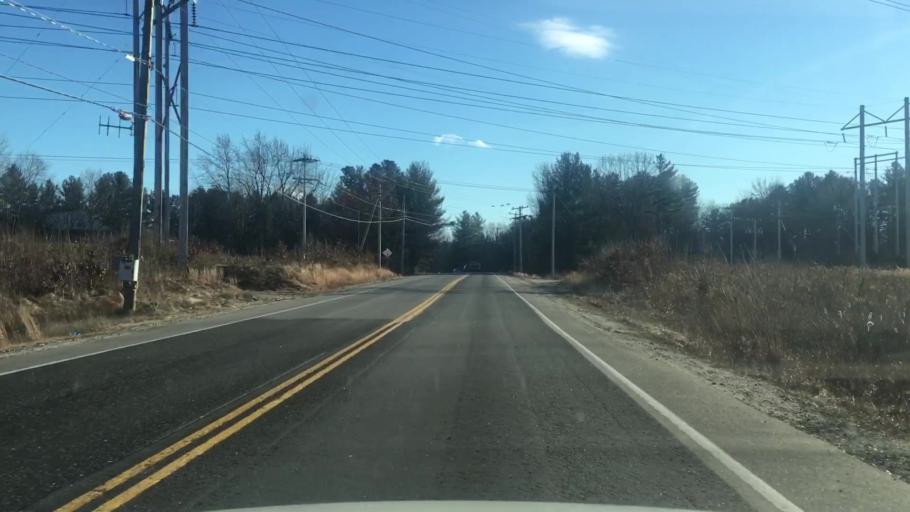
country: US
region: New Hampshire
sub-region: Rockingham County
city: Londonderry
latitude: 42.8808
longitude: -71.3816
